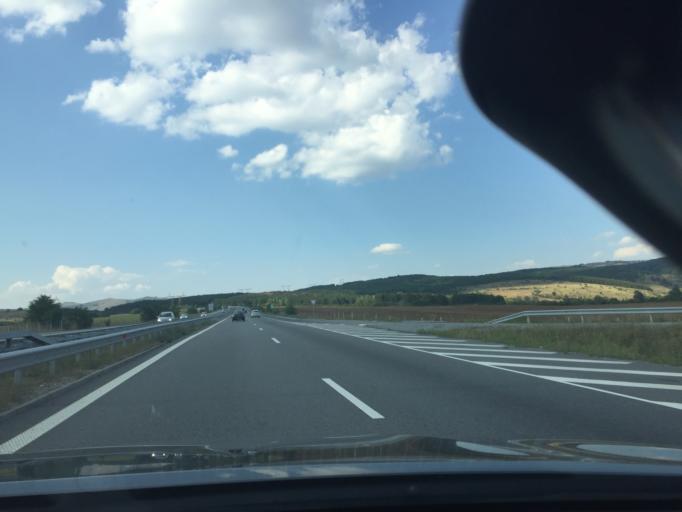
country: BG
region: Kyustendil
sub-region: Obshtina Bobovdol
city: Bobovdol
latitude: 42.4533
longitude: 23.1119
